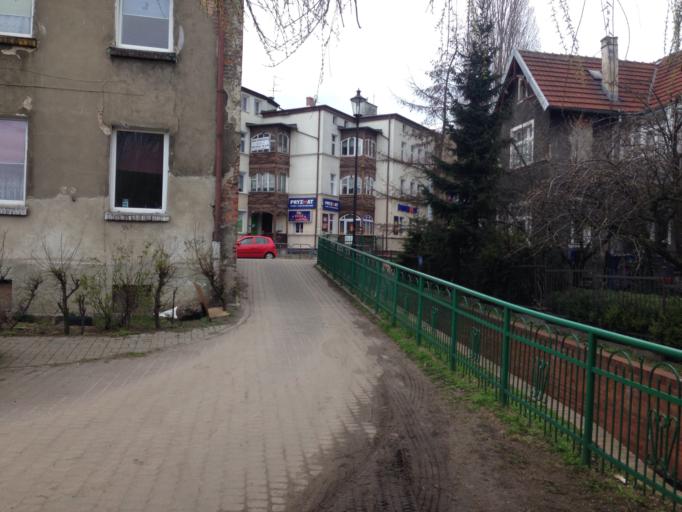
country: PL
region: Pomeranian Voivodeship
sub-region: Gdansk
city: Gdansk
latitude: 54.3810
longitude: 18.6169
